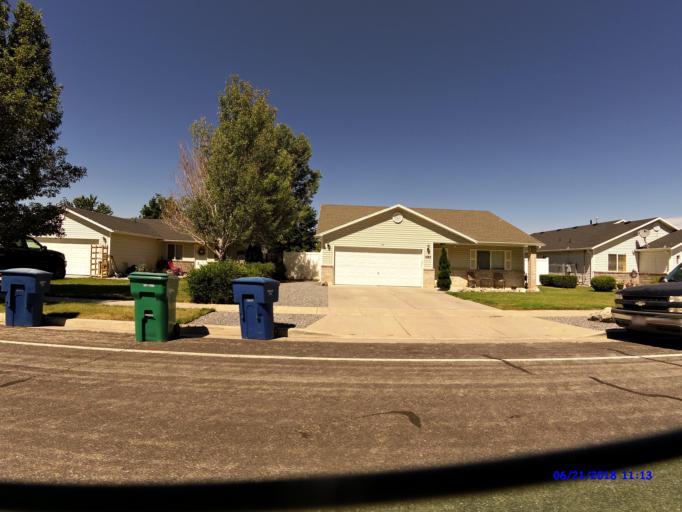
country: US
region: Utah
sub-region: Weber County
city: North Ogden
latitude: 41.2846
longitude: -111.9591
